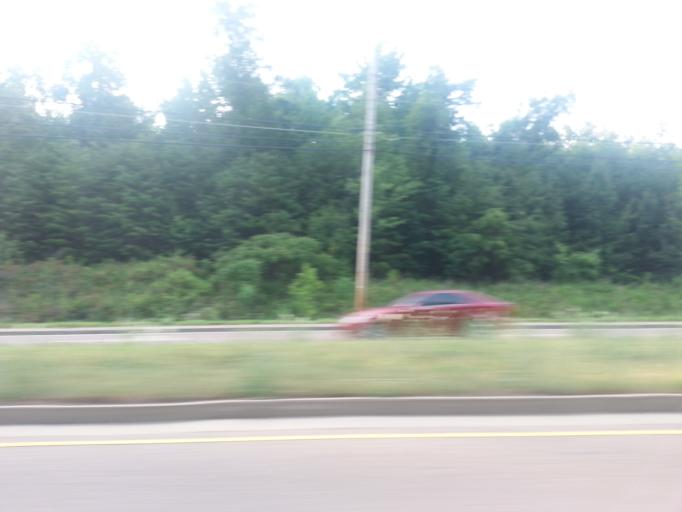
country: US
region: Tennessee
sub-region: Knox County
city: Farragut
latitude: 35.9457
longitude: -84.1051
